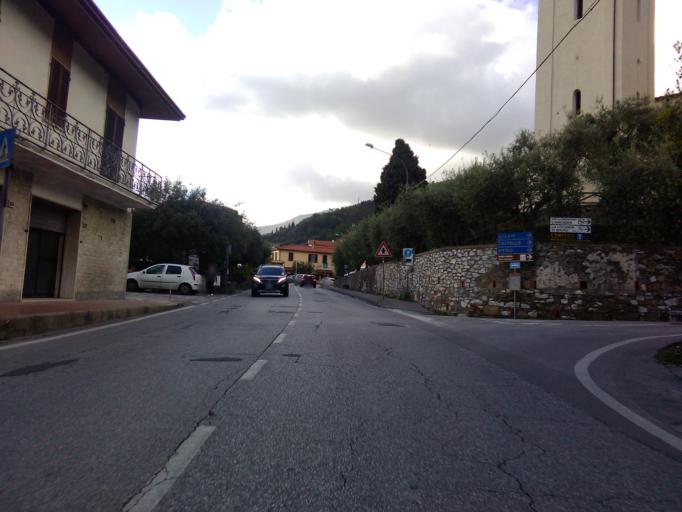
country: IT
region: Tuscany
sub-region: Provincia di Lucca
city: Seravezza
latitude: 43.9812
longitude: 10.2202
